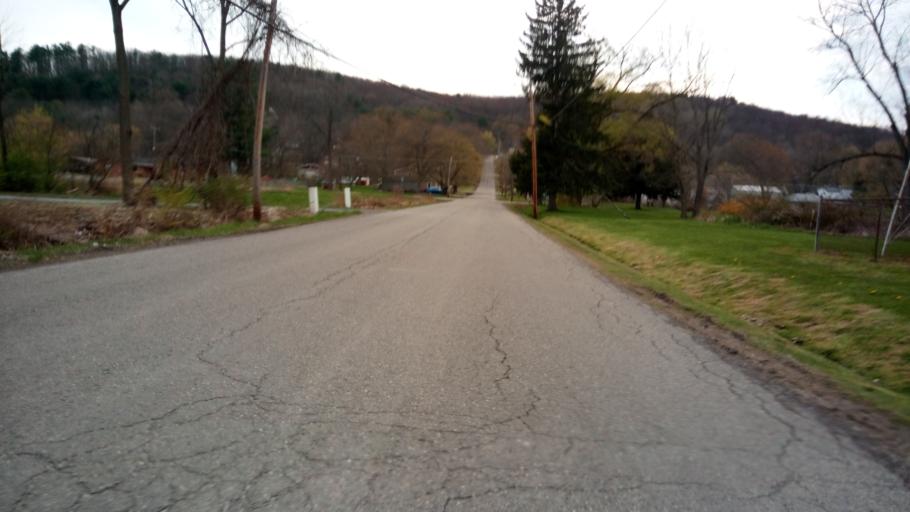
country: US
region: New York
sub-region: Chemung County
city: Southport
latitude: 42.0678
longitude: -76.8171
